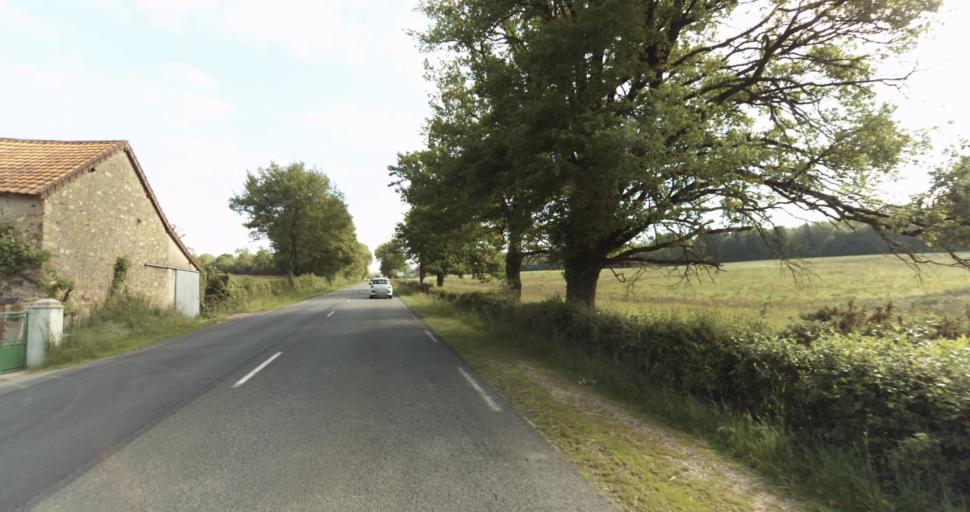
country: FR
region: Limousin
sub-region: Departement de la Haute-Vienne
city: Solignac
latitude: 45.7145
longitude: 1.2467
